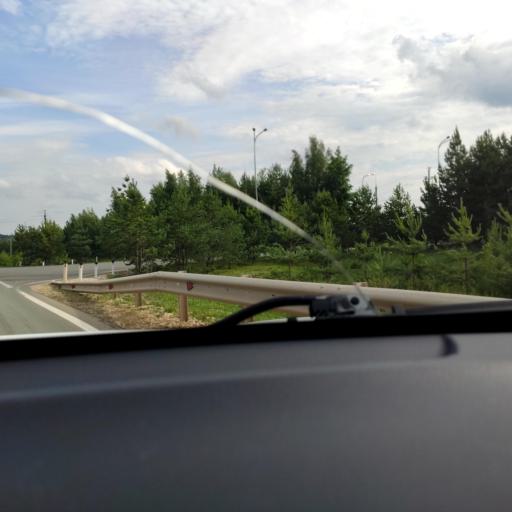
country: RU
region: Tatarstan
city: Sviyazhsk
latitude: 55.7308
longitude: 48.7432
